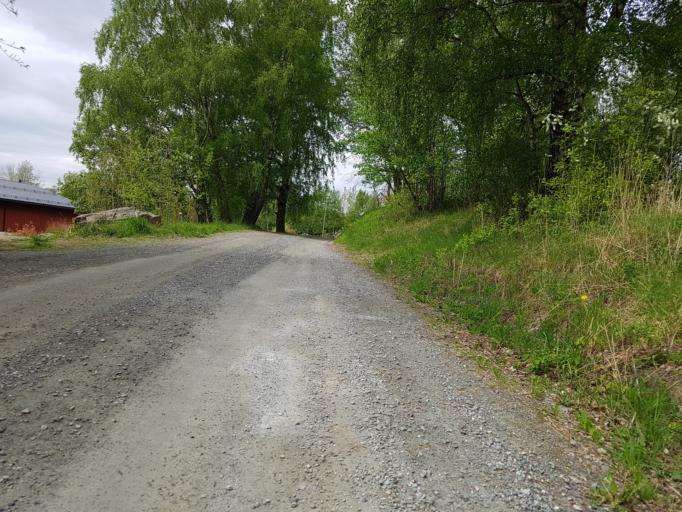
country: NO
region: Nord-Trondelag
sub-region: Levanger
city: Levanger
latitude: 63.7395
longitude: 11.2555
